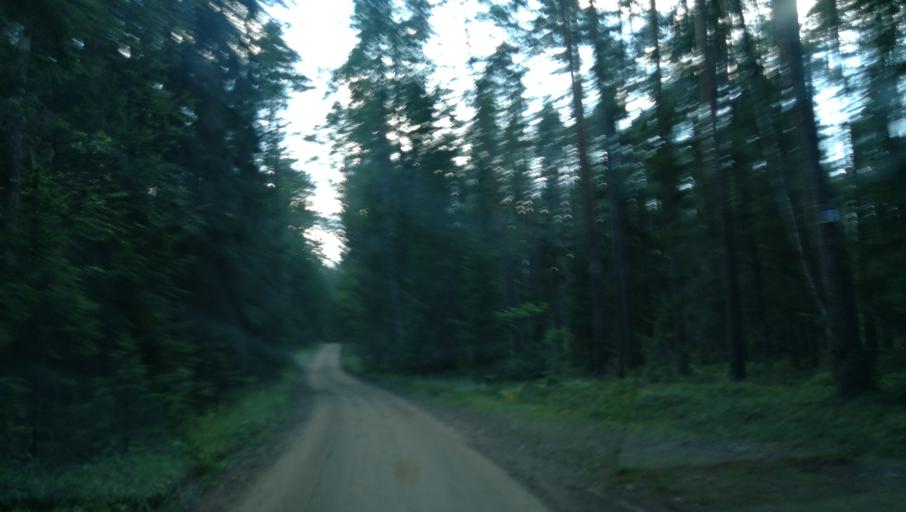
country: LV
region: Cesu Rajons
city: Cesis
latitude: 57.2900
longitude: 25.1948
